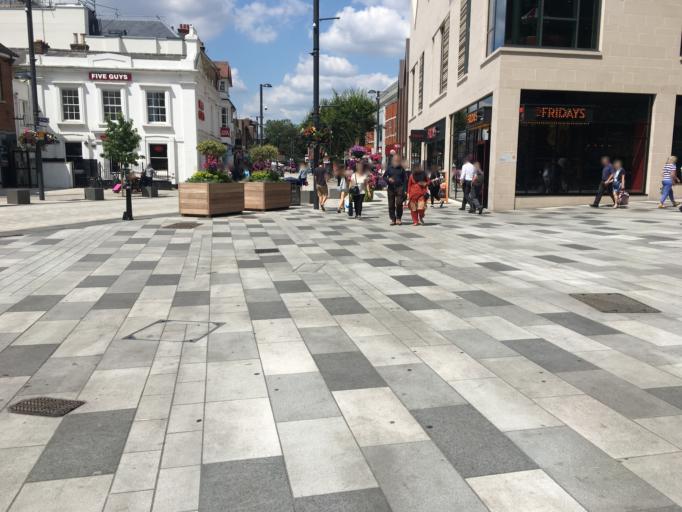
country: GB
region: England
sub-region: Hertfordshire
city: Watford
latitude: 51.6558
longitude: -0.3967
